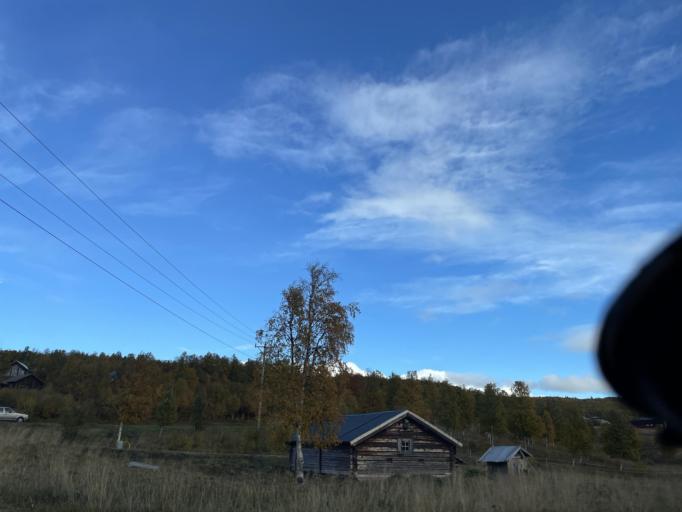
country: NO
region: Sor-Trondelag
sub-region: Tydal
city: Aas
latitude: 62.6418
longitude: 12.4301
